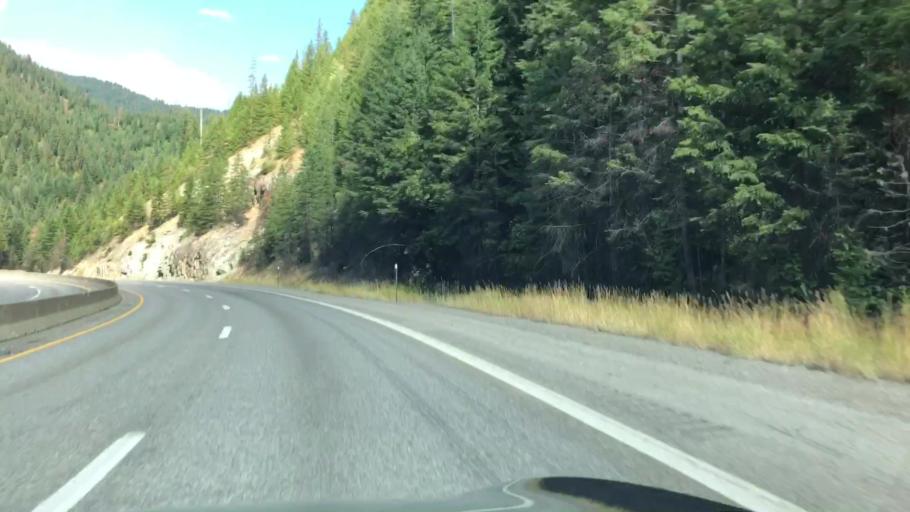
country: US
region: Idaho
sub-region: Shoshone County
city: Wallace
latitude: 47.4723
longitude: -115.8815
